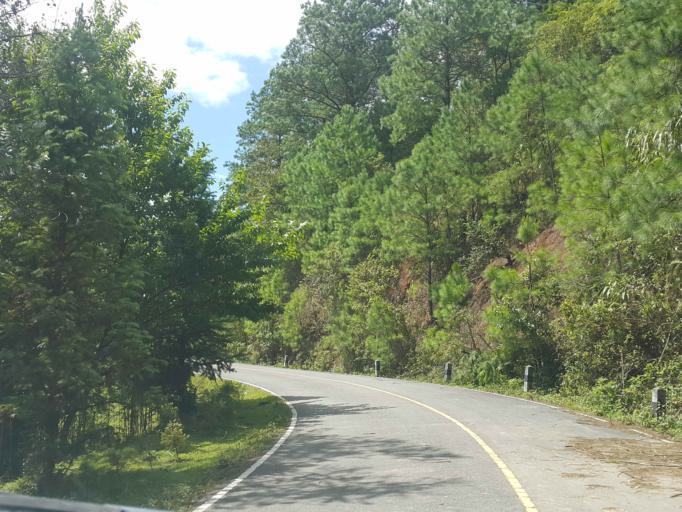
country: TH
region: Chiang Mai
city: Mae Chaem
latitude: 18.5179
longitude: 98.5310
